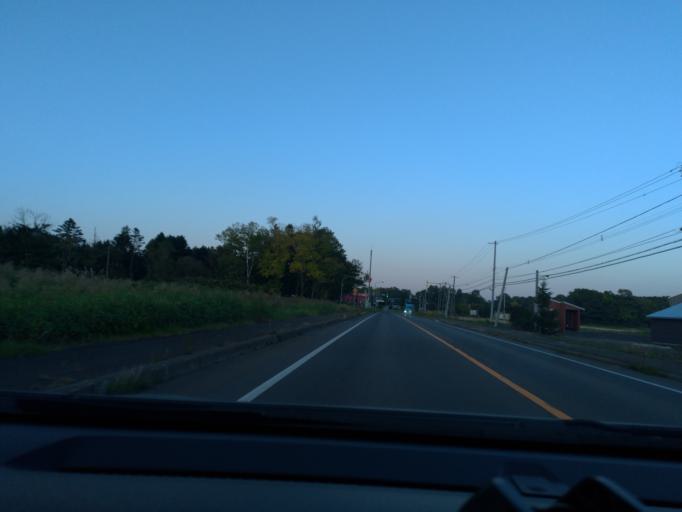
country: JP
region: Hokkaido
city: Tobetsu
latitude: 43.3236
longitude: 141.6166
